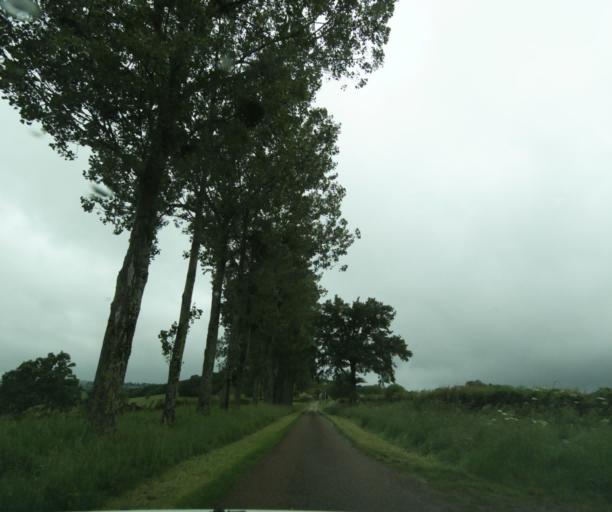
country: FR
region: Bourgogne
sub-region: Departement de Saone-et-Loire
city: Charolles
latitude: 46.3858
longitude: 4.2197
